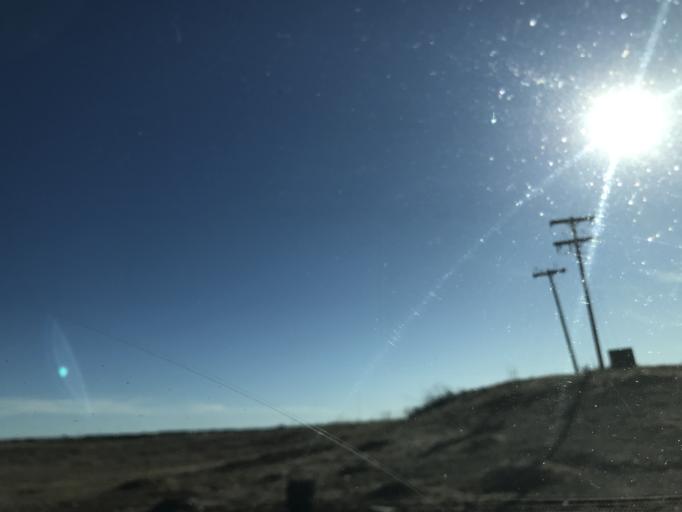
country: US
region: Colorado
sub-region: Adams County
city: Aurora
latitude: 39.7983
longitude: -104.7908
